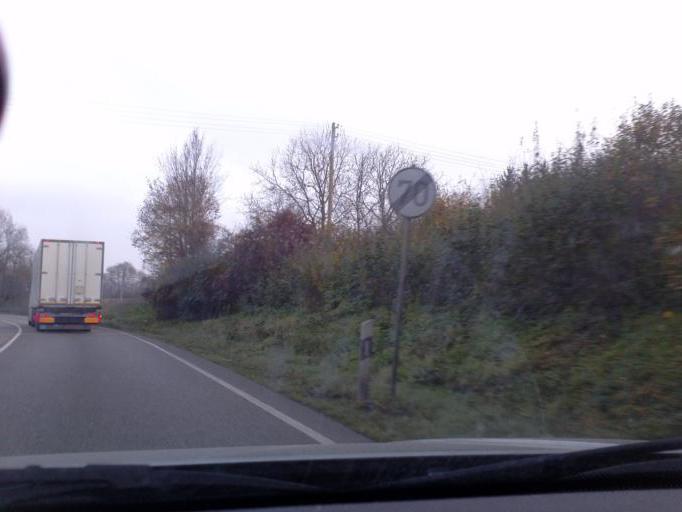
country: DE
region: Baden-Wuerttemberg
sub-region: Karlsruhe Region
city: Gondelsheim
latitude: 49.0375
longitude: 8.6734
